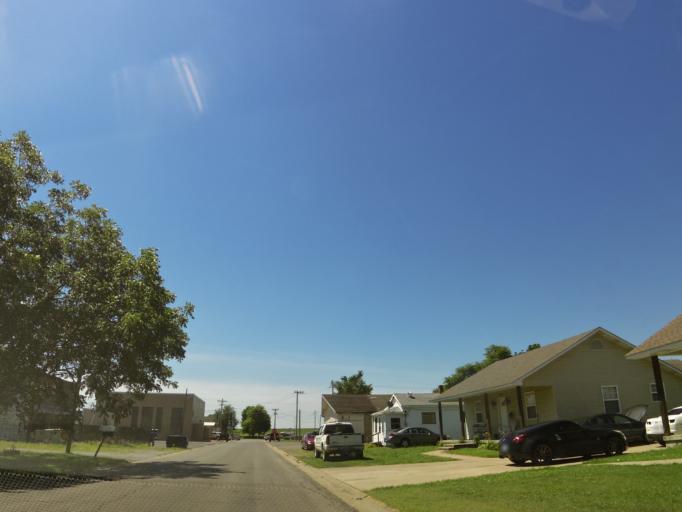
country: US
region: Missouri
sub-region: New Madrid County
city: New Madrid
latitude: 36.5859
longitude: -89.5283
